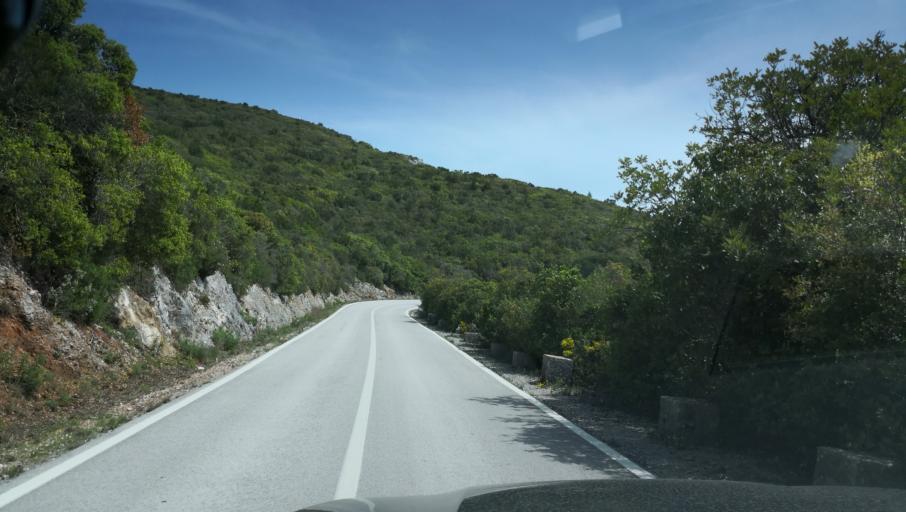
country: PT
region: Setubal
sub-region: Sesimbra
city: Sesimbra
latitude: 38.4626
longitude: -9.0075
